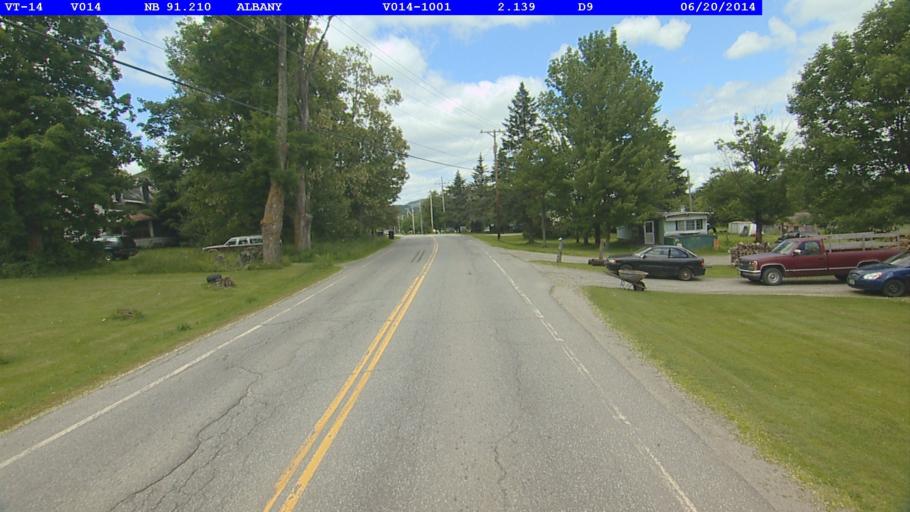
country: US
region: Vermont
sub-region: Caledonia County
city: Hardwick
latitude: 44.7318
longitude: -72.3794
